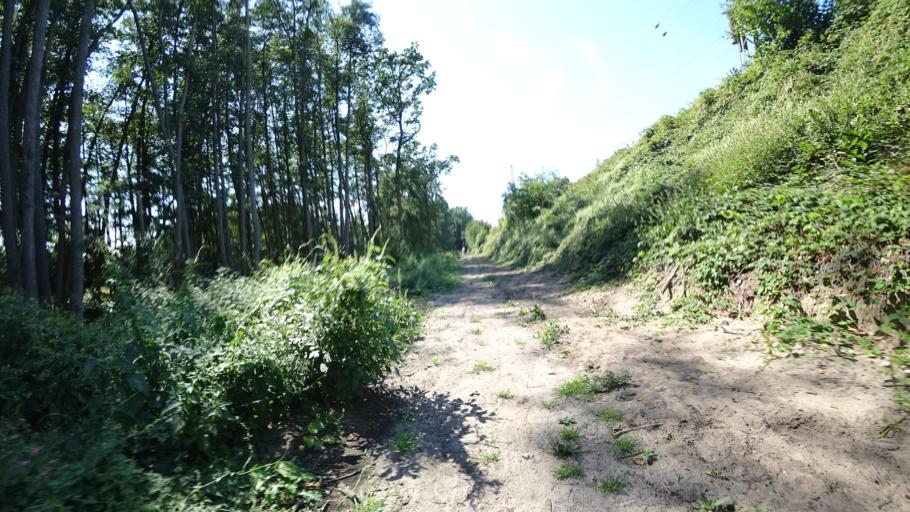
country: DE
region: North Rhine-Westphalia
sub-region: Regierungsbezirk Detmold
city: Steinhagen
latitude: 51.9475
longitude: 8.4509
